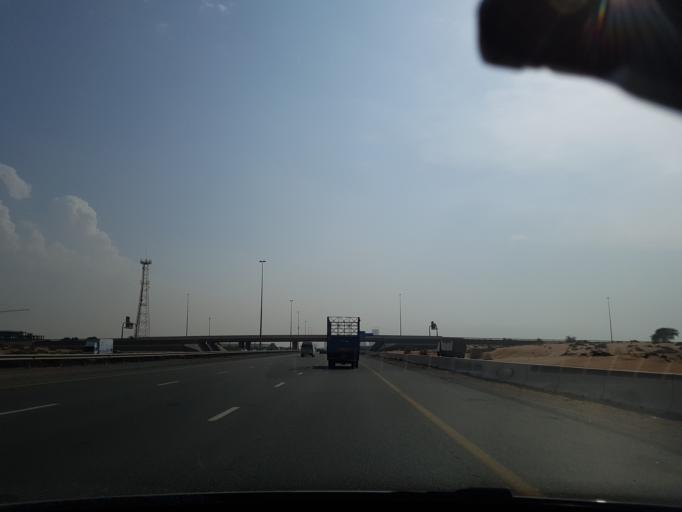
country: AE
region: Umm al Qaywayn
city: Umm al Qaywayn
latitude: 25.4285
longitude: 55.5938
